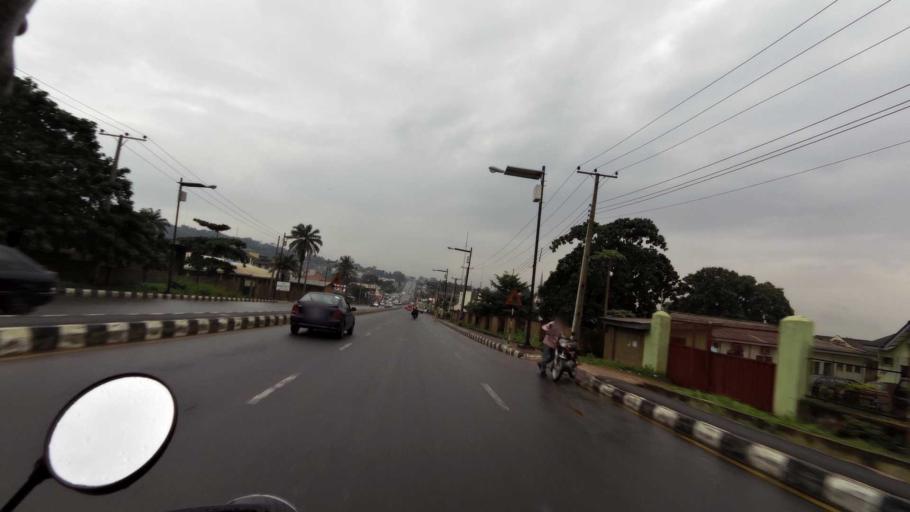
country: NG
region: Oyo
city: Ibadan
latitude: 7.3986
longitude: 3.9068
